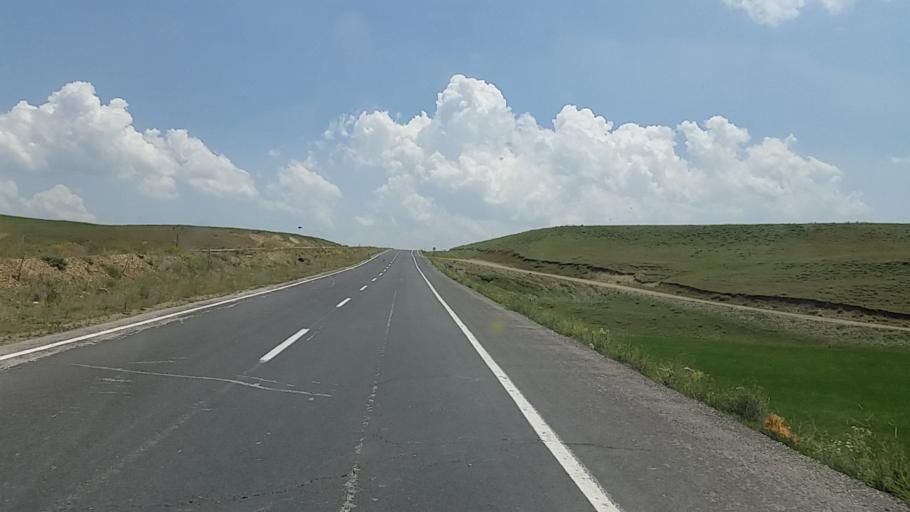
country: TR
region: Agri
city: Taslicay
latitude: 39.6270
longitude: 43.4503
